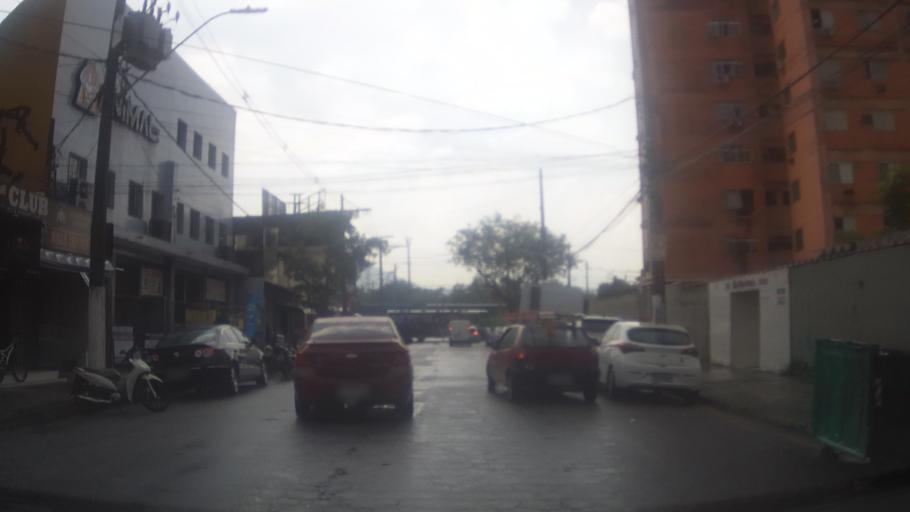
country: BR
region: Sao Paulo
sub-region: Santos
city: Santos
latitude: -23.9318
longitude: -46.3491
